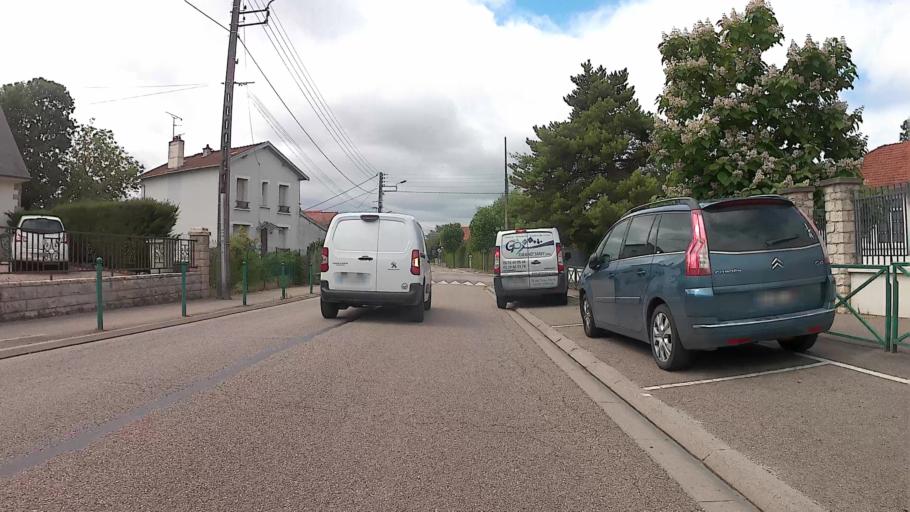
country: FR
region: Lorraine
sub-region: Departement de la Meuse
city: Verdun
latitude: 49.1513
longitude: 5.3949
